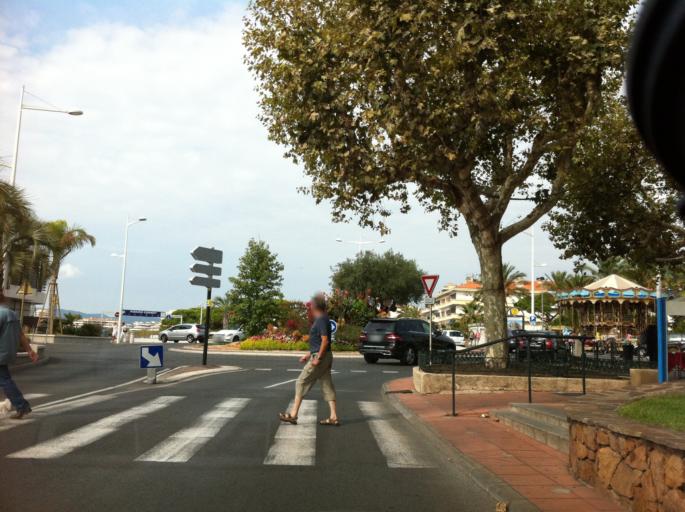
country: FR
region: Provence-Alpes-Cote d'Azur
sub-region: Departement du Var
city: Saint-Raphael
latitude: 43.4244
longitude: 6.7648
